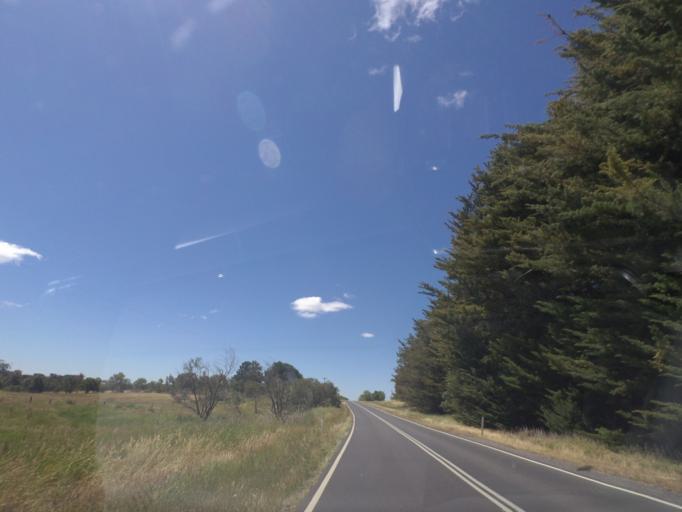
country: AU
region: Victoria
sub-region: Mount Alexander
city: Castlemaine
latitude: -37.2424
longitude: 144.3254
